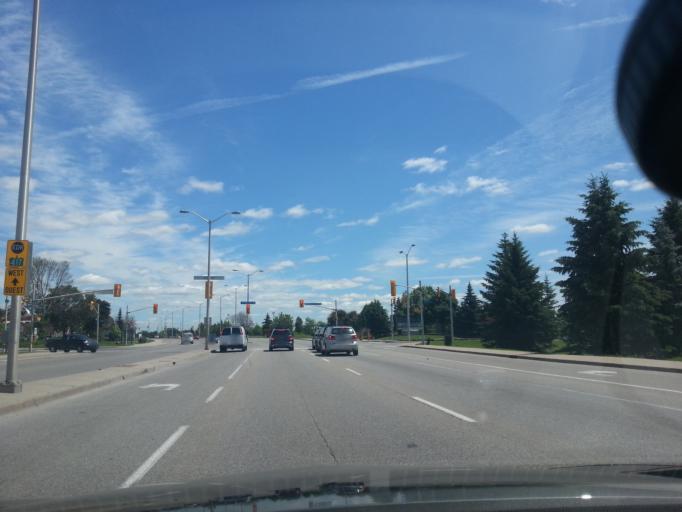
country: CA
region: Ontario
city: Bells Corners
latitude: 45.2973
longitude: -75.9018
